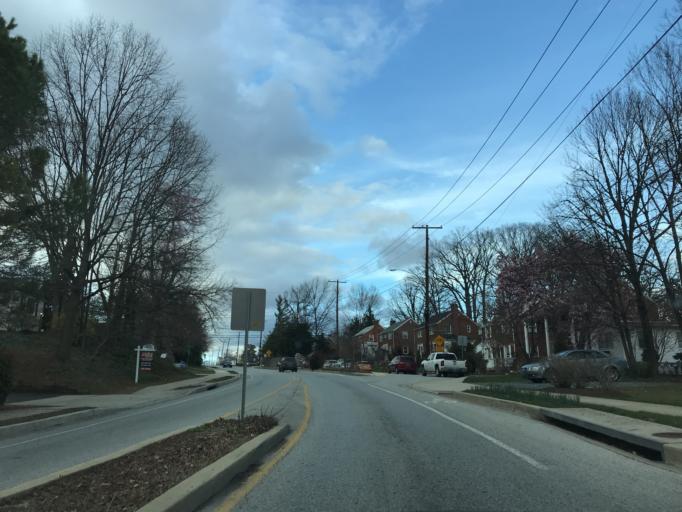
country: US
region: Maryland
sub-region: Prince George's County
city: Langley Park
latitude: 38.9881
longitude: -76.9942
